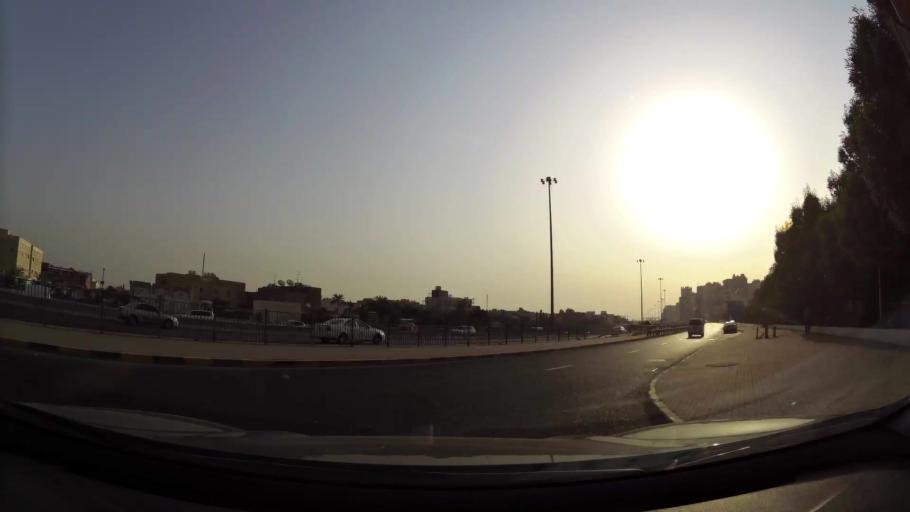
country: KW
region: Muhafazat Hawalli
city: As Salimiyah
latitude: 29.3253
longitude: 48.0688
